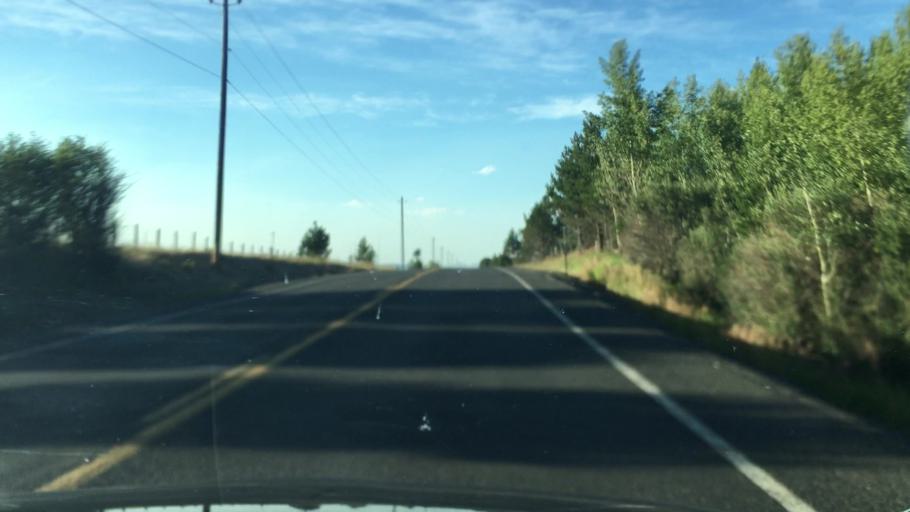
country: US
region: Idaho
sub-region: Valley County
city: McCall
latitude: 44.7949
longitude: -116.0782
